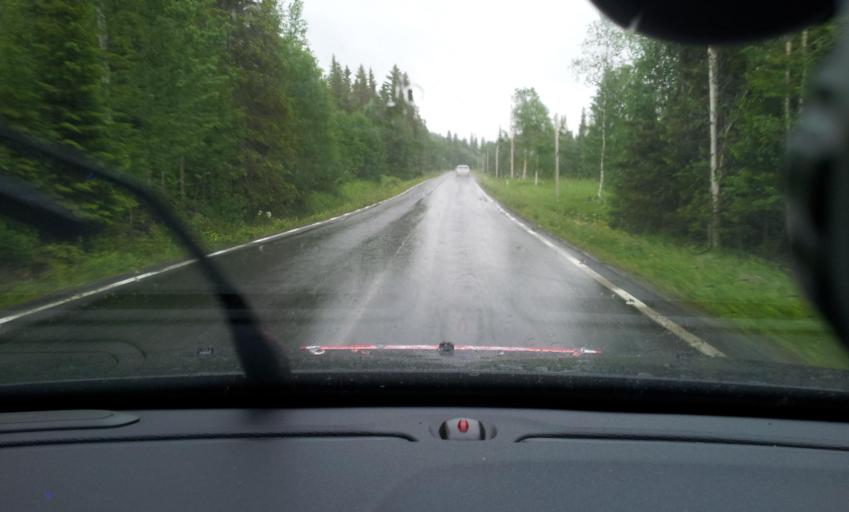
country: SE
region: Jaemtland
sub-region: Are Kommun
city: Are
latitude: 63.3142
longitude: 13.1580
